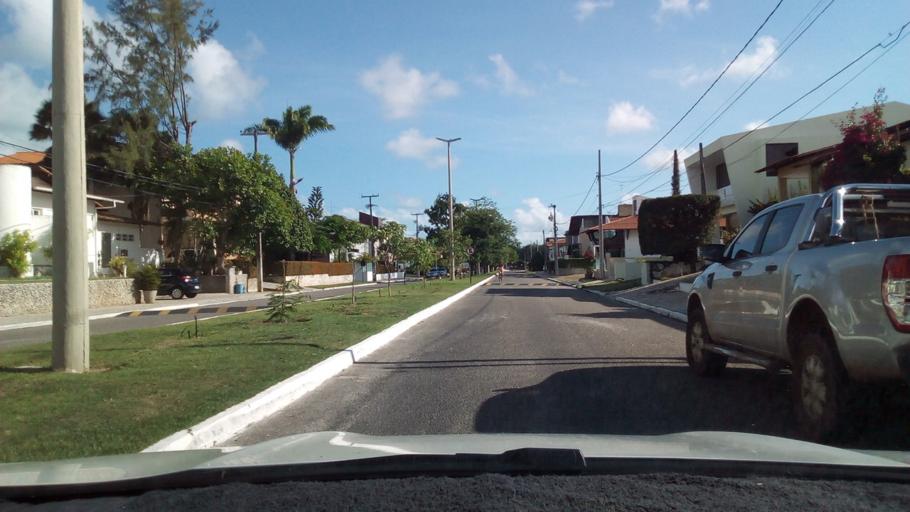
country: BR
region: Paraiba
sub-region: Joao Pessoa
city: Joao Pessoa
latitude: -7.1577
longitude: -34.8069
